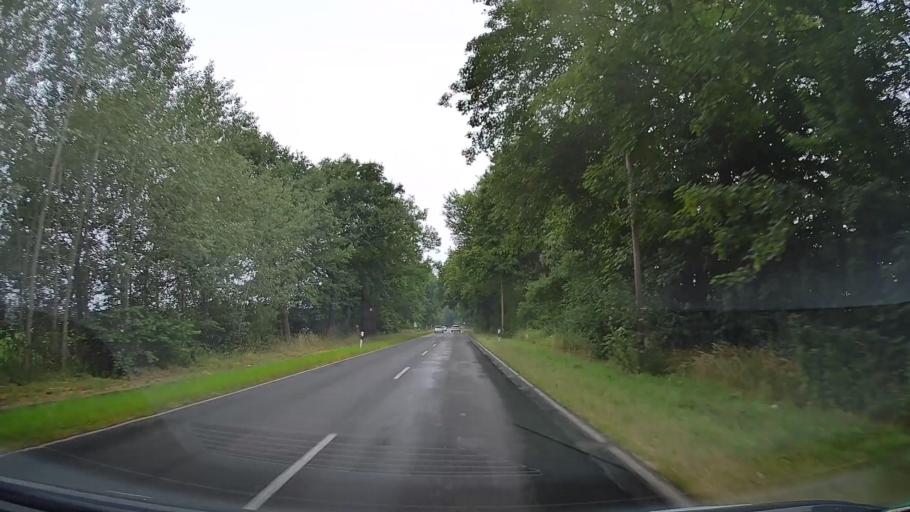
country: DE
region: Lower Saxony
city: Lohne
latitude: 52.6147
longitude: 8.2916
